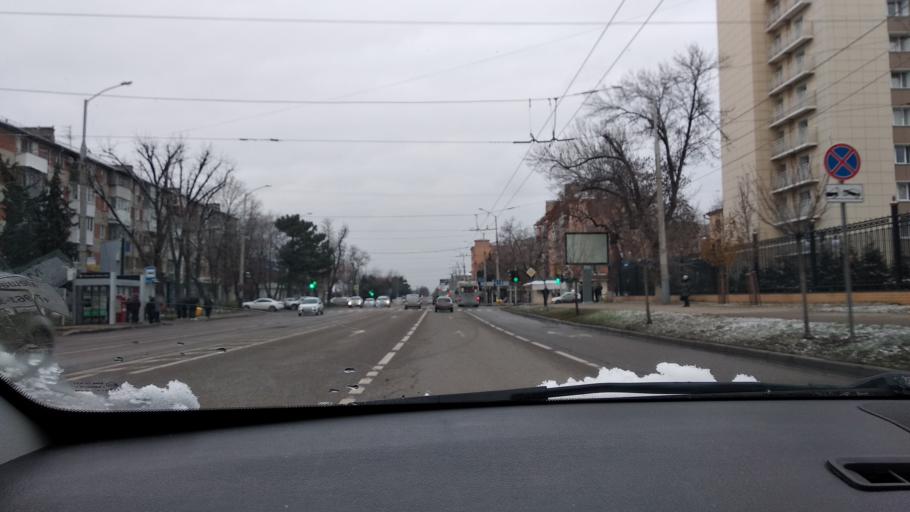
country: RU
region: Krasnodarskiy
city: Krasnodar
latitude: 45.0422
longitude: 38.9631
